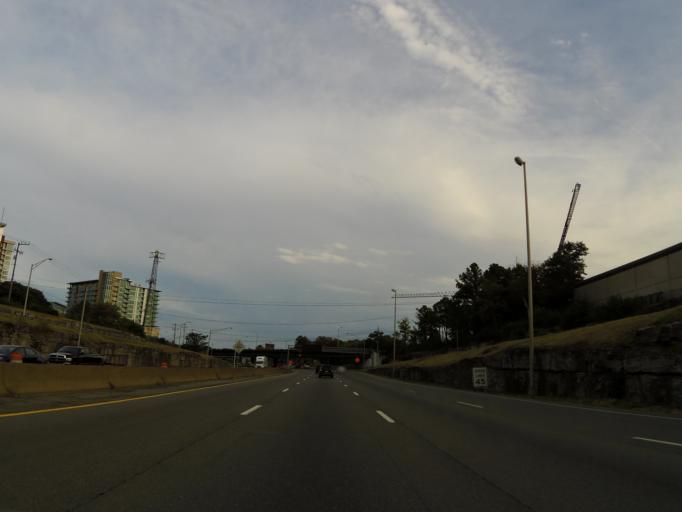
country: US
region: Tennessee
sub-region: Davidson County
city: Nashville
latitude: 36.1531
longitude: -86.7876
